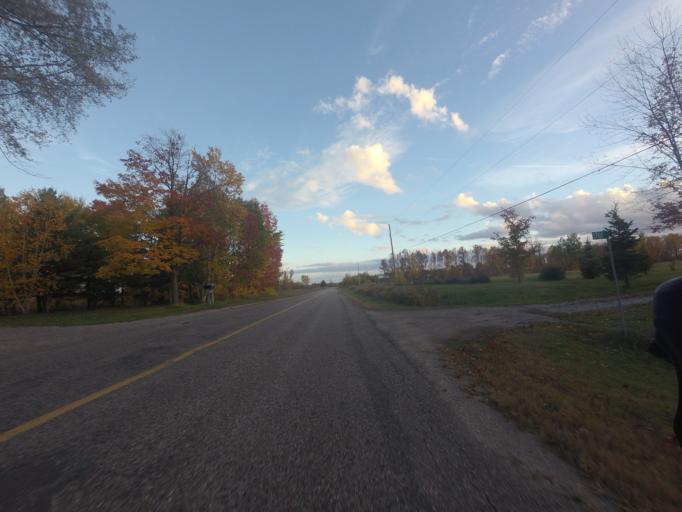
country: CA
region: Ontario
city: Renfrew
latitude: 45.4397
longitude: -76.9643
